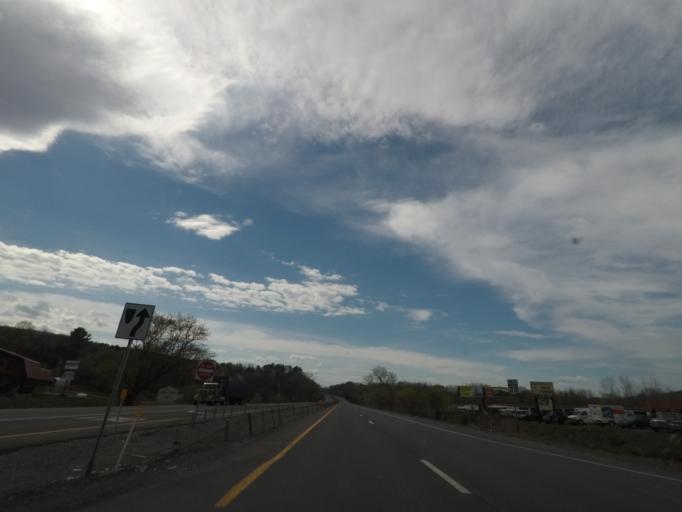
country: US
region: New York
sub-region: Greene County
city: Jefferson Heights
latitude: 42.2523
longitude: -73.9068
